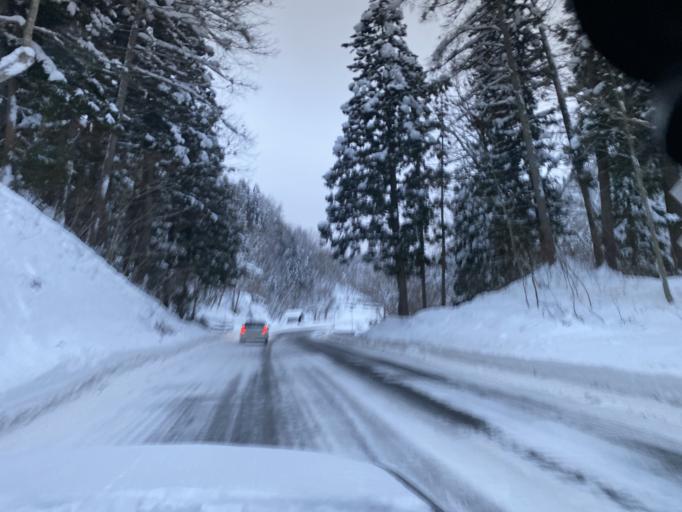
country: JP
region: Nagano
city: Omachi
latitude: 36.5933
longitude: 137.8881
